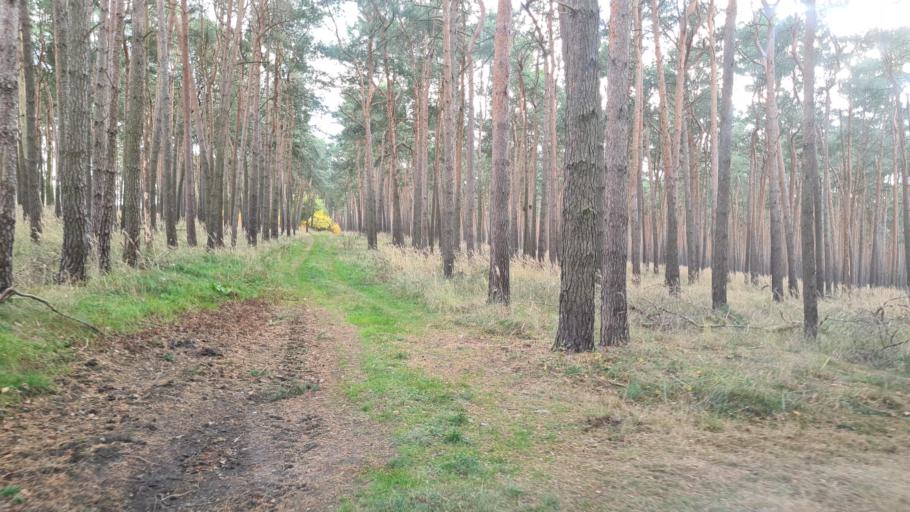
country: DE
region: Saxony-Anhalt
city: Zahna
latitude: 51.9707
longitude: 12.8137
